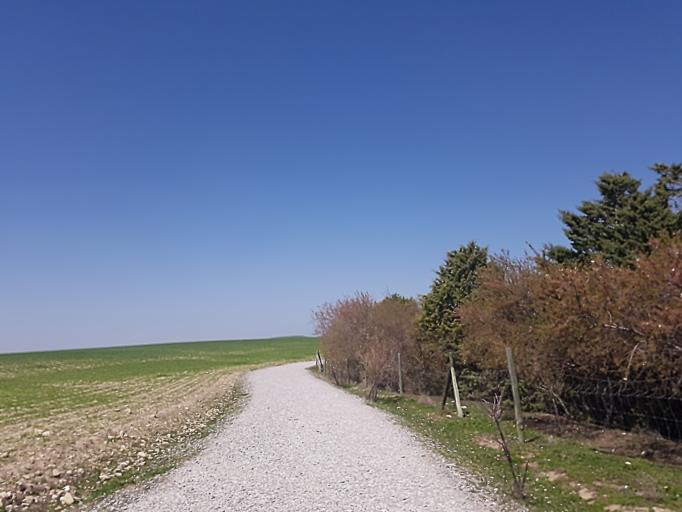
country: ES
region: Castille and Leon
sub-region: Provincia de Segovia
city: Segovia
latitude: 40.9487
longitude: -4.1339
